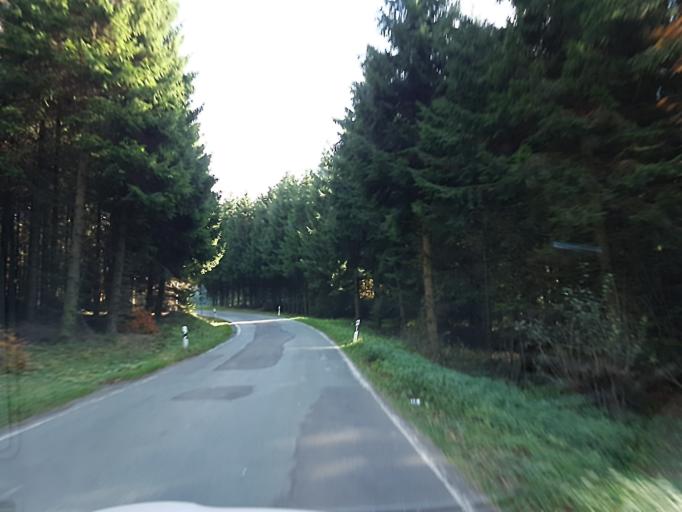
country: DE
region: North Rhine-Westphalia
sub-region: Regierungsbezirk Arnsberg
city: Drolshagen
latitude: 51.1013
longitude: 7.7709
